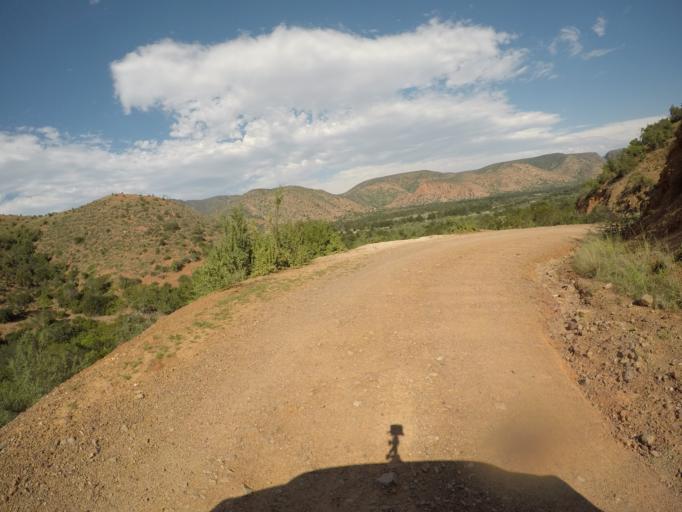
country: ZA
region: Eastern Cape
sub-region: Cacadu District Municipality
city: Kareedouw
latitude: -33.6582
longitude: 24.4010
